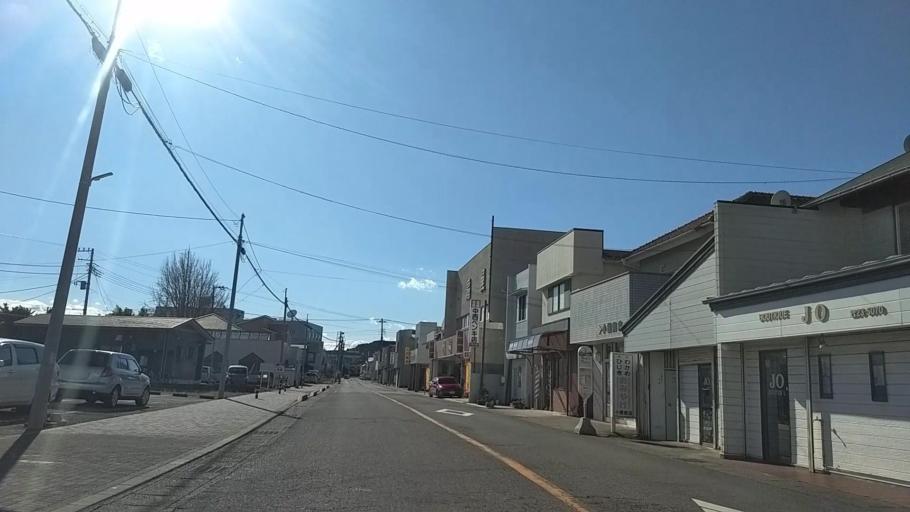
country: JP
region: Chiba
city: Tateyama
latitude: 34.9889
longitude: 139.8624
